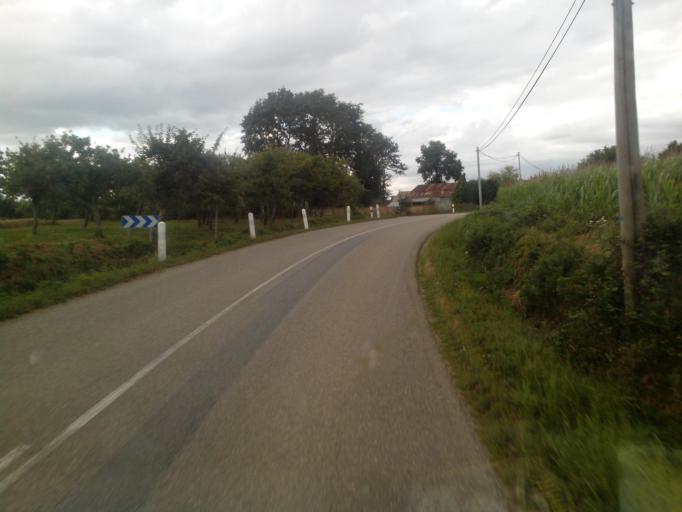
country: FR
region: Brittany
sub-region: Departement d'Ille-et-Vilaine
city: Maxent
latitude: 47.9745
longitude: -2.0224
